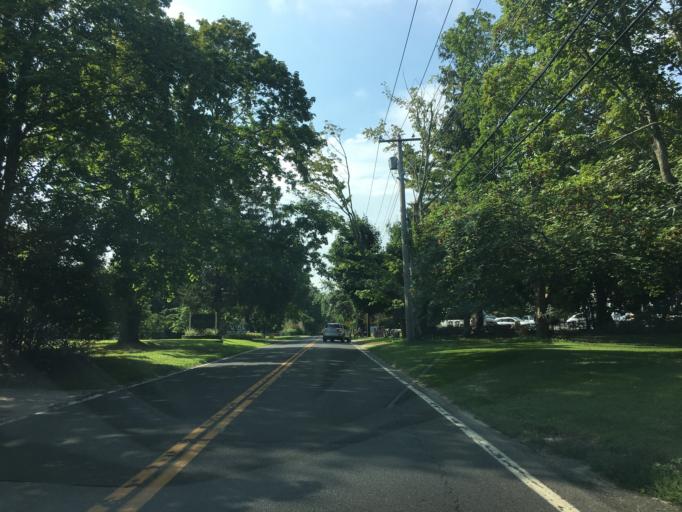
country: US
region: New York
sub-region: Suffolk County
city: Shelter Island
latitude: 41.0665
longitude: -72.3314
